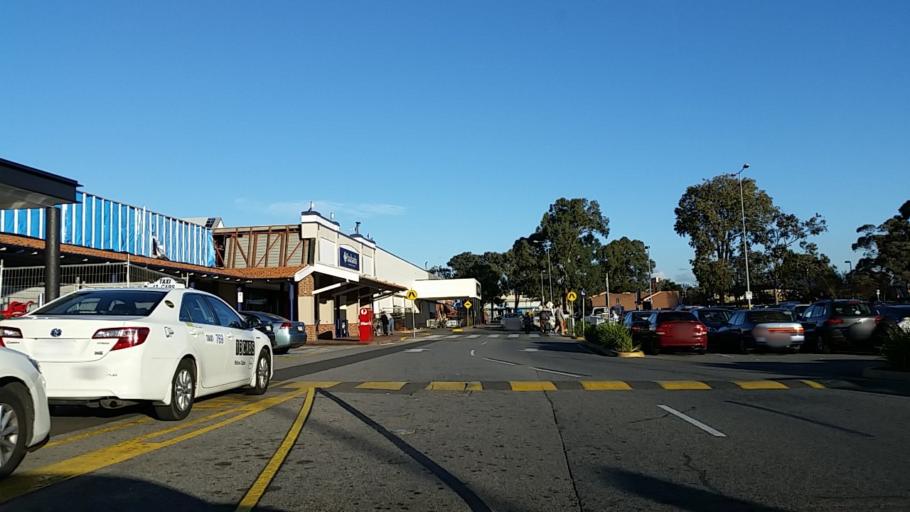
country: AU
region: South Australia
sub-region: Salisbury
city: Salisbury
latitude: -34.7605
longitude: 138.6454
